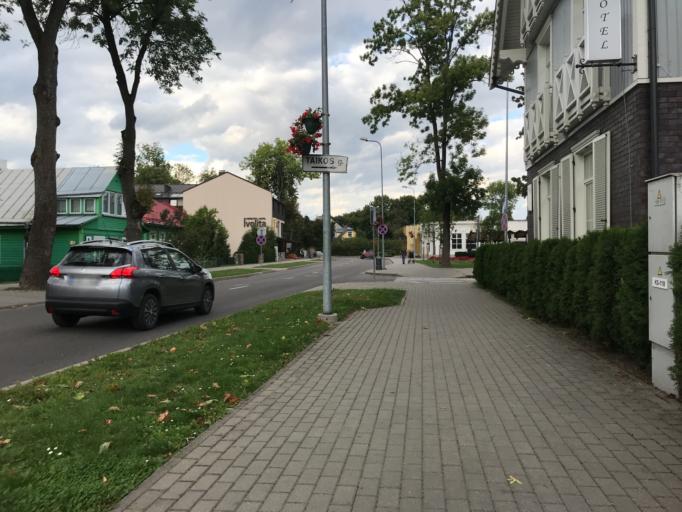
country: LT
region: Alytaus apskritis
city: Druskininkai
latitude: 54.0180
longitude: 23.9722
